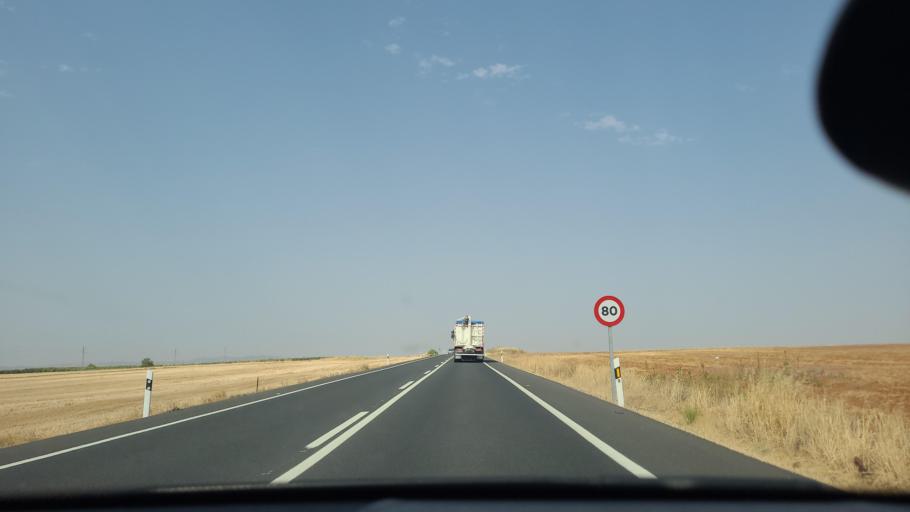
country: ES
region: Extremadura
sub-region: Provincia de Badajoz
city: Berlanga
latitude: 38.2665
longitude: -5.7736
